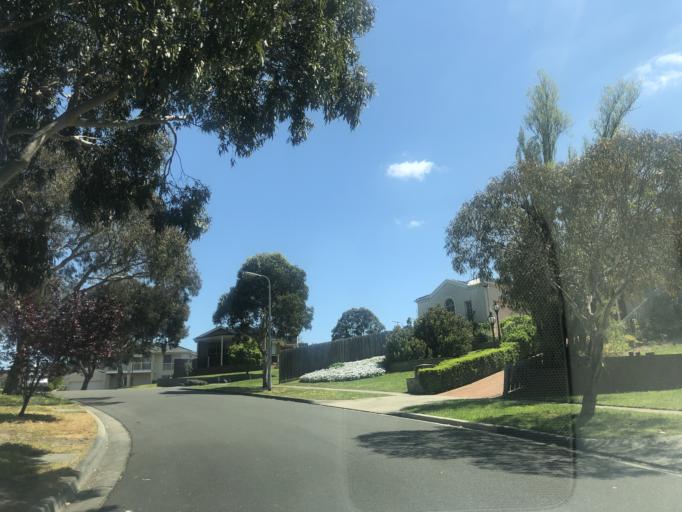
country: AU
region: Victoria
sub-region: Monash
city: Mulgrave
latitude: -37.9119
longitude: 145.1919
